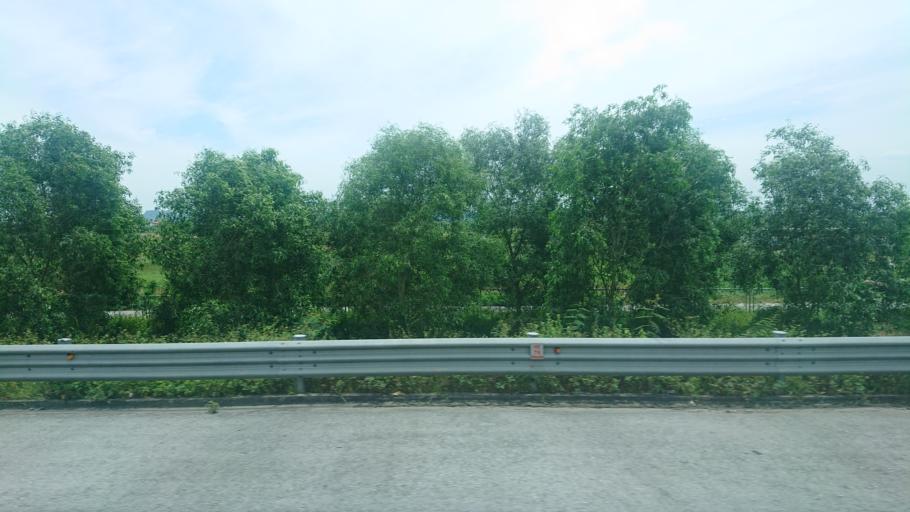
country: VN
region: Hai Phong
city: An Lao
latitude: 20.7851
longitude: 106.5620
